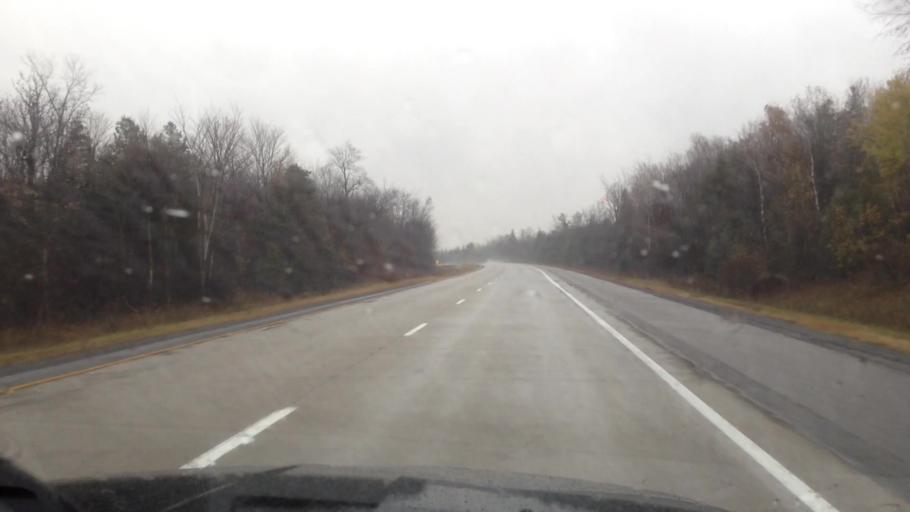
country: CA
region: Ontario
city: Casselman
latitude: 45.3802
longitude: -74.8173
